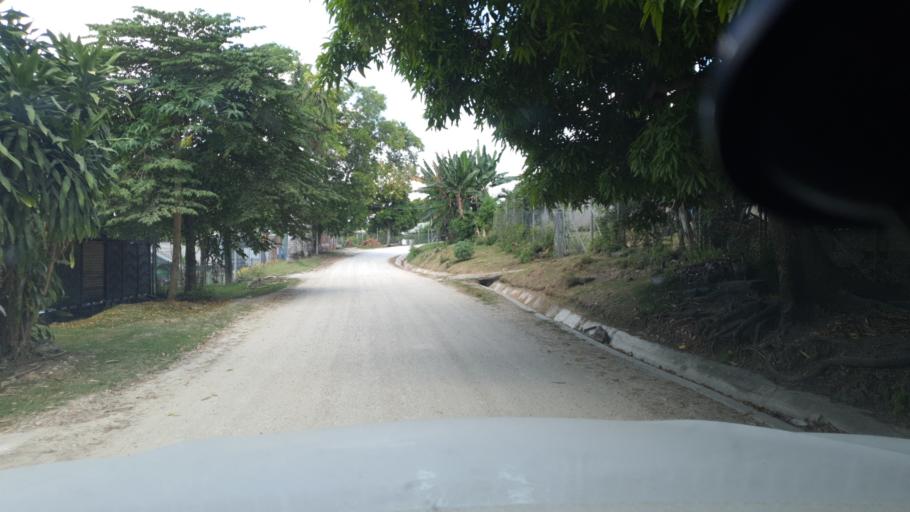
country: SB
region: Guadalcanal
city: Honiara
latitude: -9.4293
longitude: 159.9355
